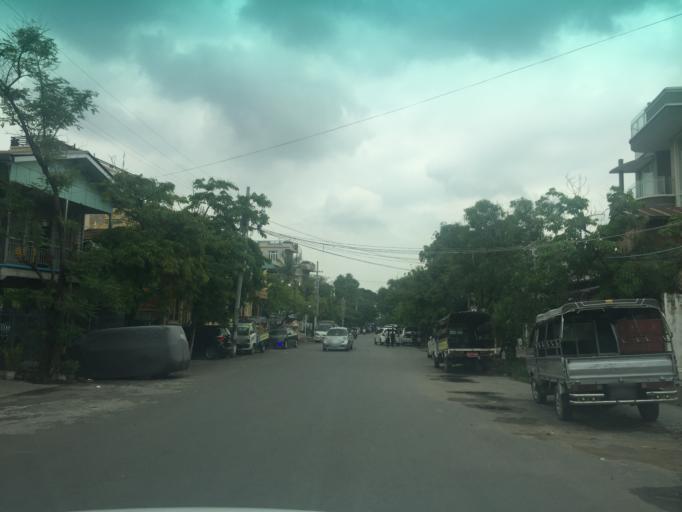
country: MM
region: Mandalay
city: Mandalay
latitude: 21.9653
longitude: 96.0784
